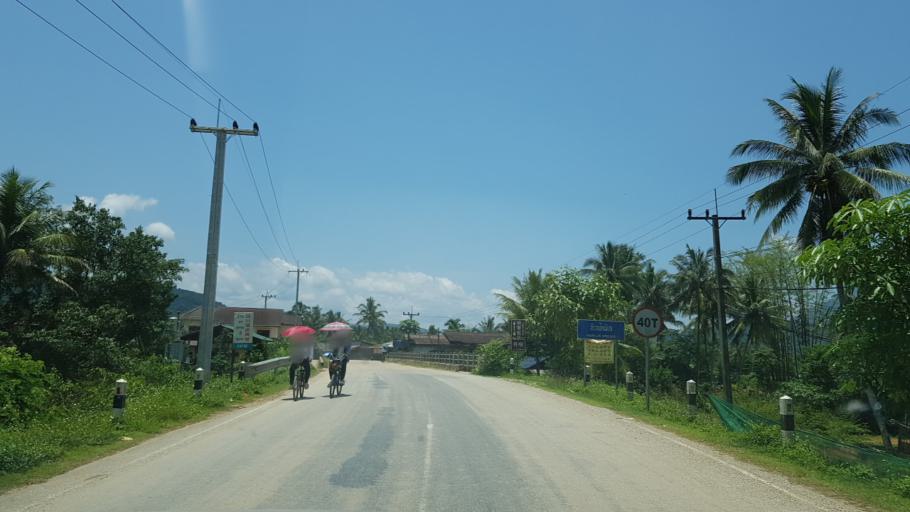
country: LA
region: Vientiane
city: Muang Kasi
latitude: 19.2346
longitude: 102.2527
